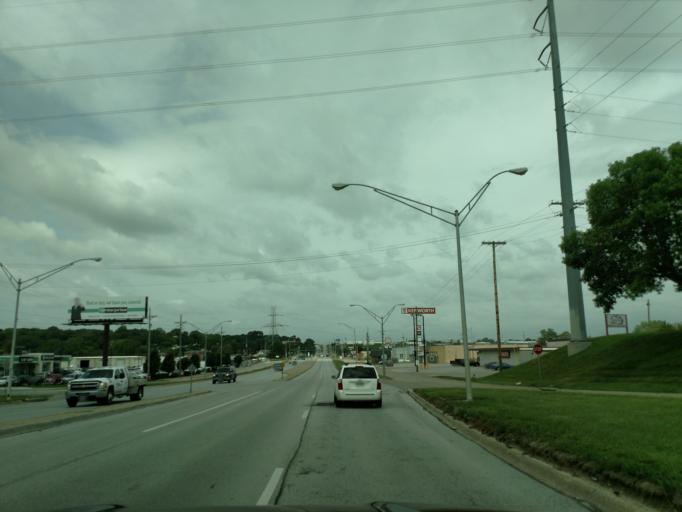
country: US
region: Nebraska
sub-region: Douglas County
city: Ralston
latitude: 41.2124
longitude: -96.0275
